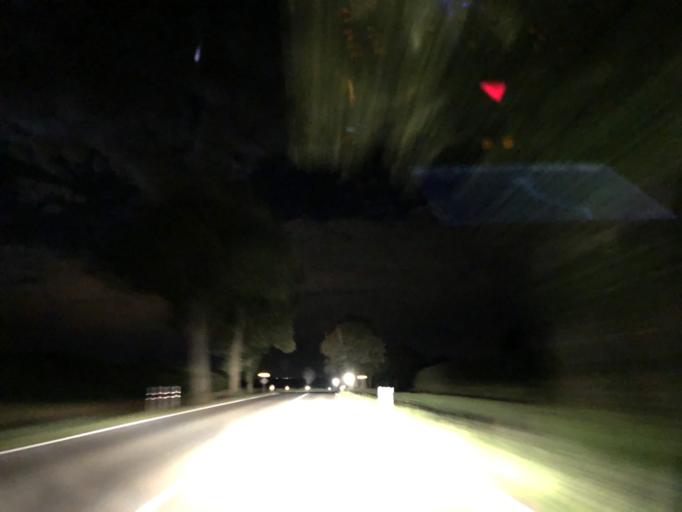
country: DE
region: Bavaria
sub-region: Upper Bavaria
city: Moosinning
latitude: 48.2573
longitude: 11.8612
